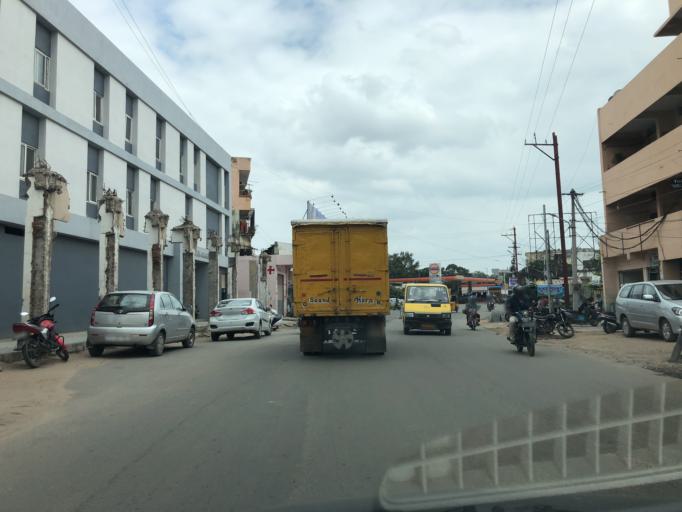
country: IN
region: Telangana
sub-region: Rangareddi
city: Quthbullapur
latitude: 17.4689
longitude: 78.4803
